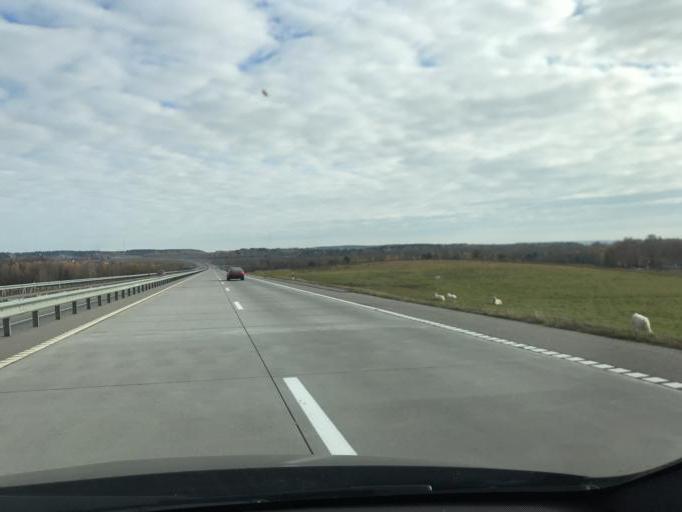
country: BY
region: Minsk
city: Pyatryshki
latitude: 54.0549
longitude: 27.2028
